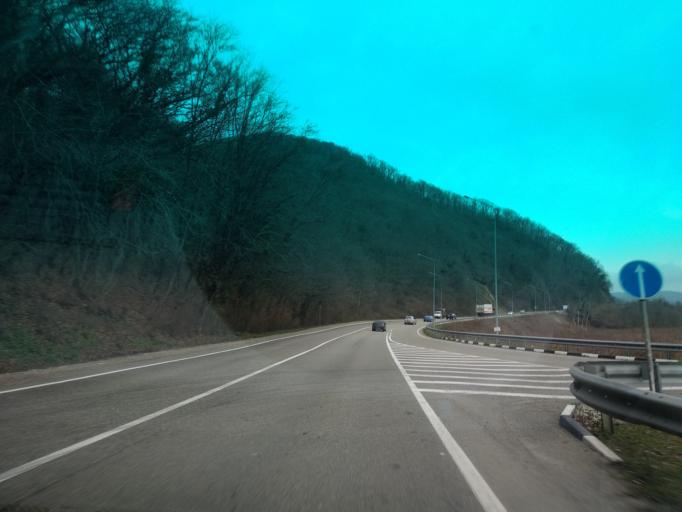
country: RU
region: Krasnodarskiy
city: Ol'ginka
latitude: 44.2175
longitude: 38.8943
